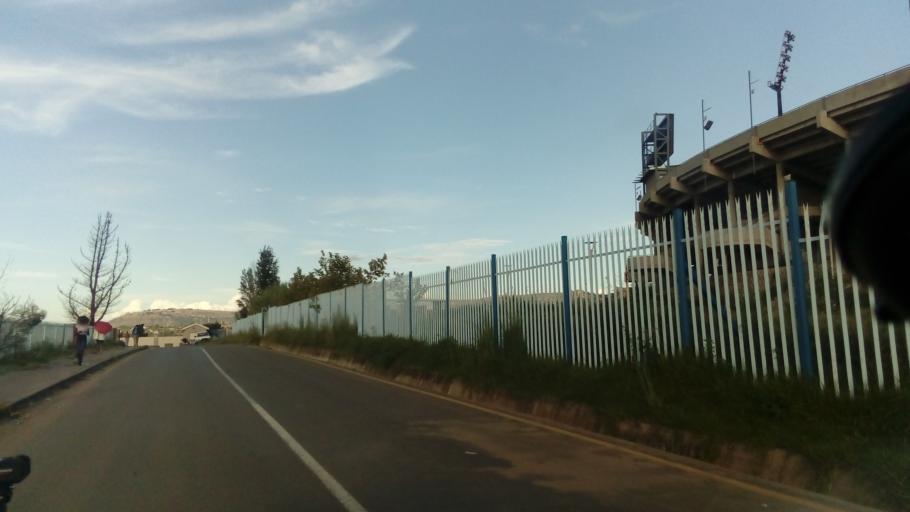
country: LS
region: Maseru
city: Maseru
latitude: -29.3099
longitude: 27.5005
